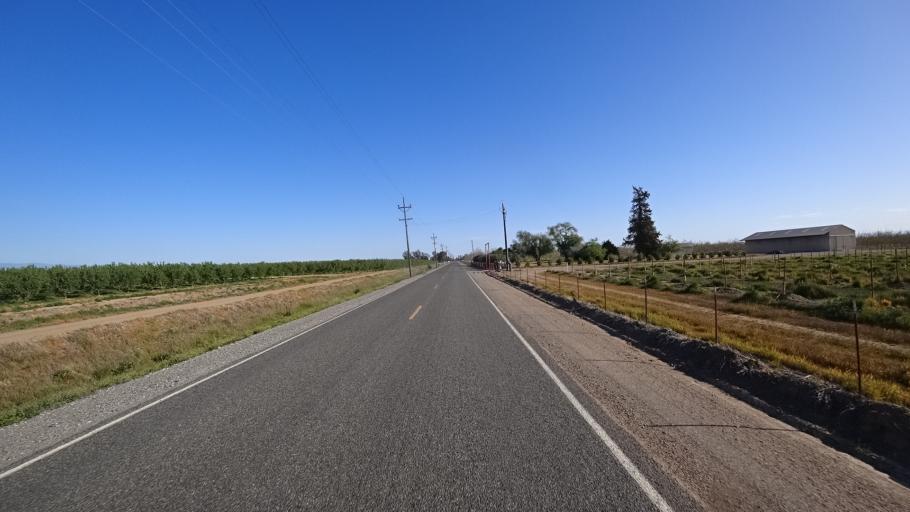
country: US
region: California
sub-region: Glenn County
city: Orland
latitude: 39.6849
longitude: -122.1780
